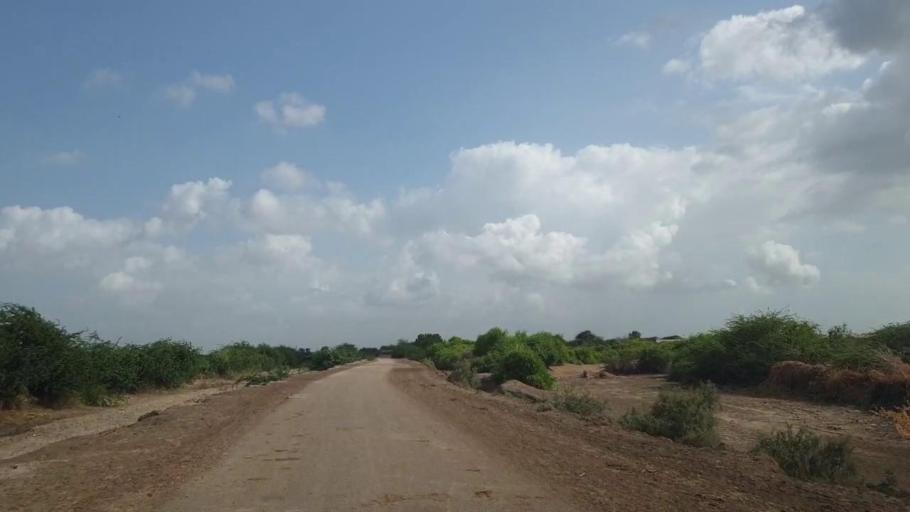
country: PK
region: Sindh
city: Kadhan
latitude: 24.5524
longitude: 69.0635
